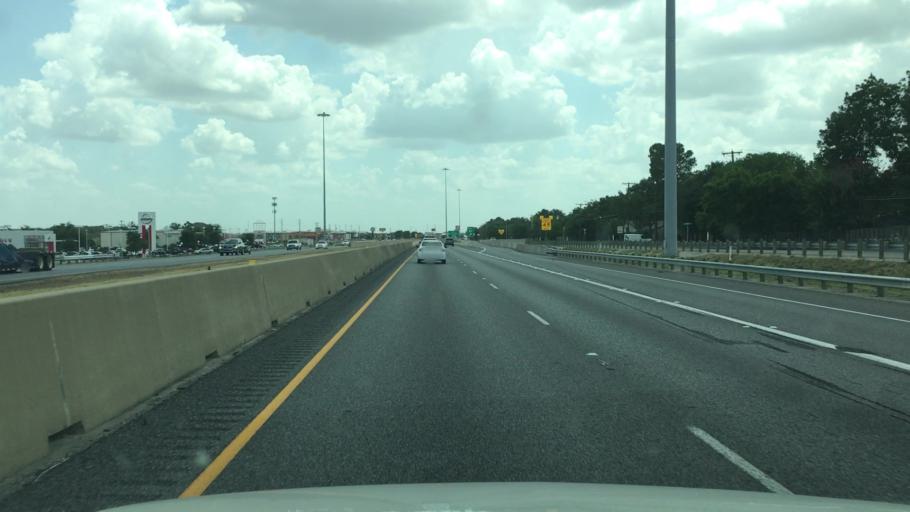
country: US
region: Texas
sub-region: Hunt County
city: Greenville
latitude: 33.1073
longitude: -96.1028
